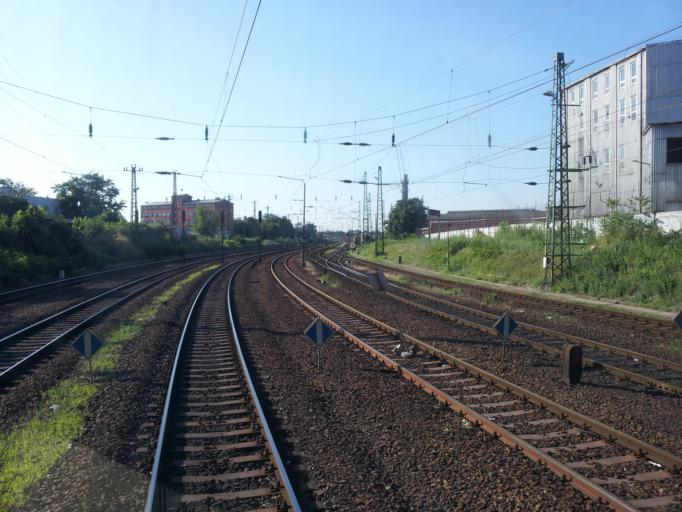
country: HU
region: Budapest
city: Budapest XIV. keruelet
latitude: 47.4991
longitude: 19.0981
